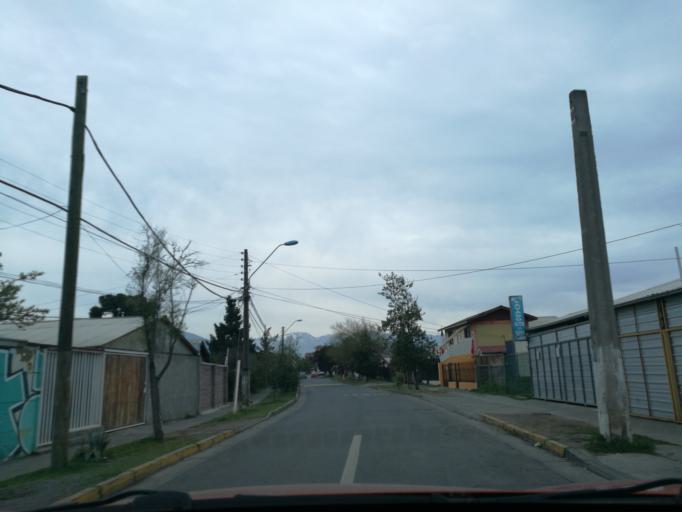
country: CL
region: O'Higgins
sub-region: Provincia de Cachapoal
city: Machali
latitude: -34.1749
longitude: -70.6915
